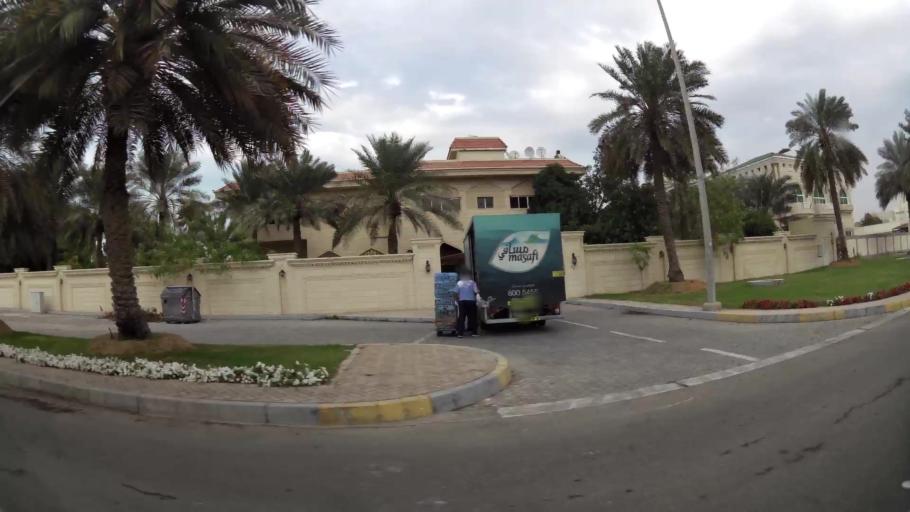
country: AE
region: Abu Dhabi
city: Abu Dhabi
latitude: 24.4514
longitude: 54.3511
